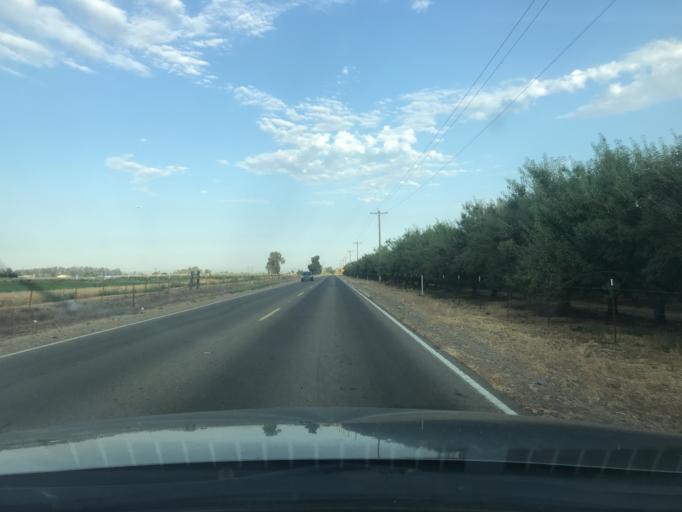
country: US
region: California
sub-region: Merced County
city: Atwater
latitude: 37.3608
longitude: -120.5352
